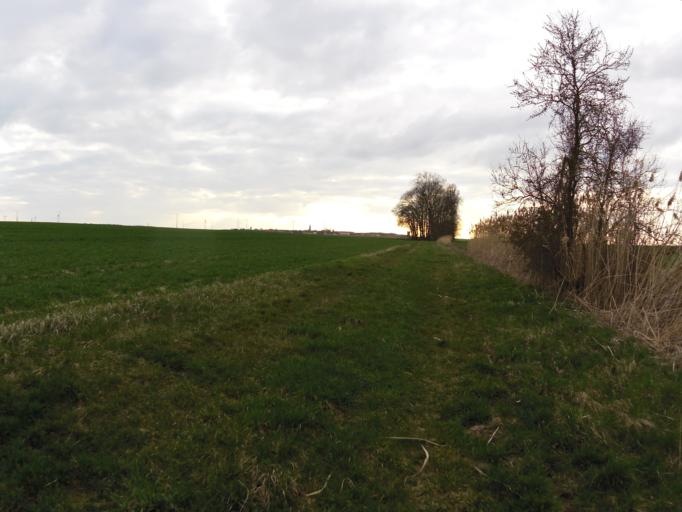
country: DE
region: Bavaria
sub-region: Regierungsbezirk Unterfranken
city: Biebelried
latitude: 49.7491
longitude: 10.0873
